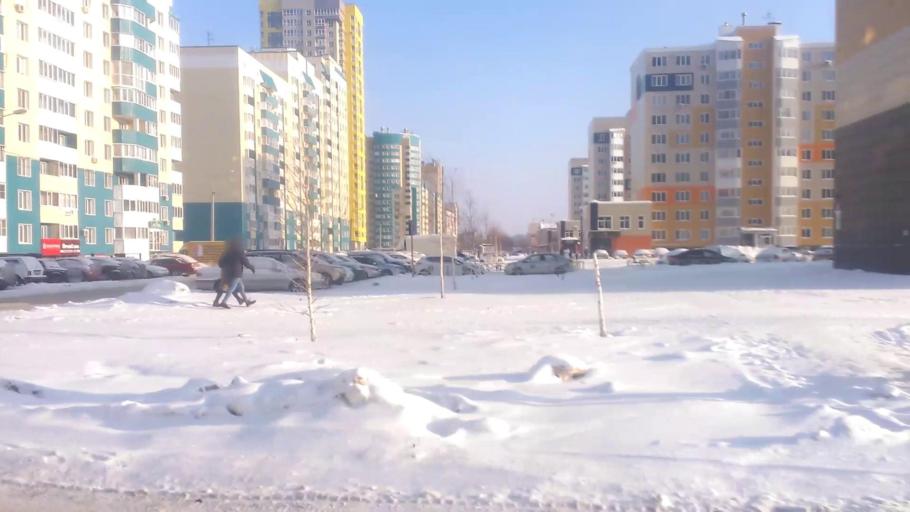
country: RU
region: Altai Krai
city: Novosilikatnyy
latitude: 53.3407
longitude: 83.6546
